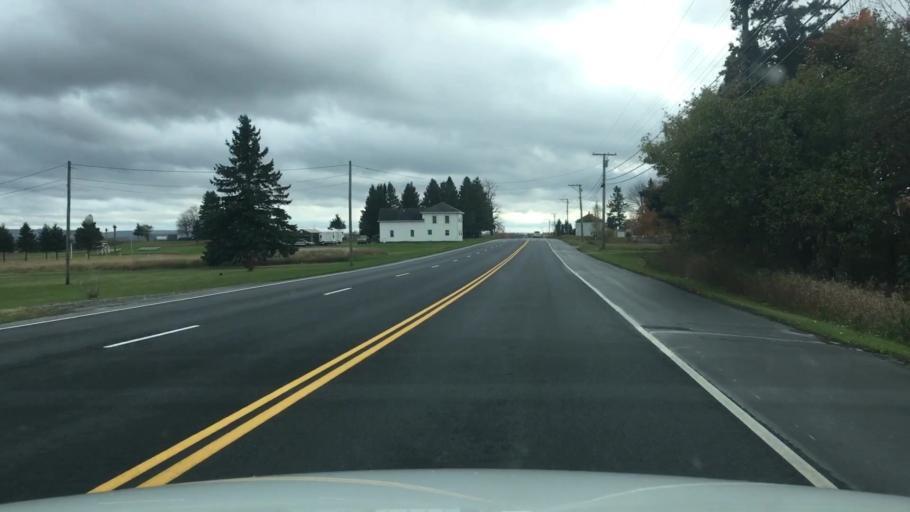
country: US
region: Maine
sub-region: Aroostook County
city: Houlton
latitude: 46.2240
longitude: -67.8410
